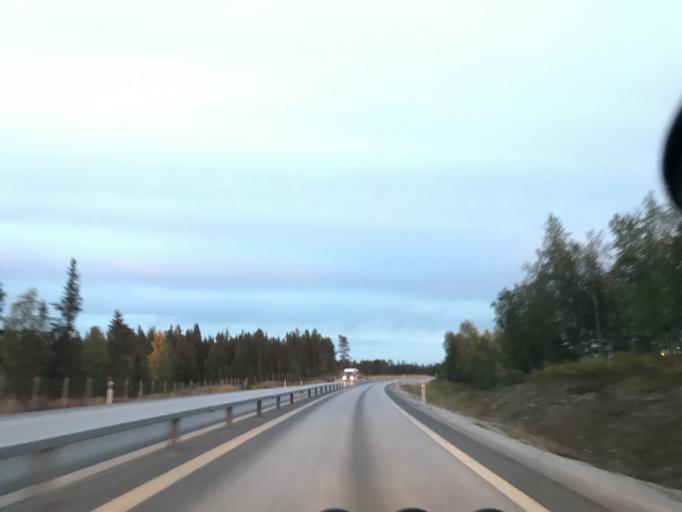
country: SE
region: Norrbotten
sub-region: Gallivare Kommun
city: Malmberget
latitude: 67.6589
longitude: 21.0041
